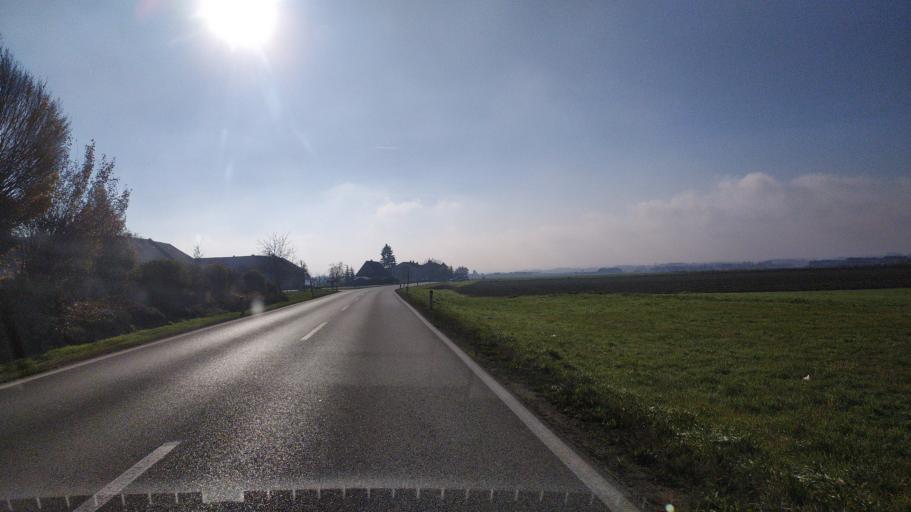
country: AT
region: Upper Austria
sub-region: Politischer Bezirk Perg
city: Perg
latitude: 48.2313
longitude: 14.6231
